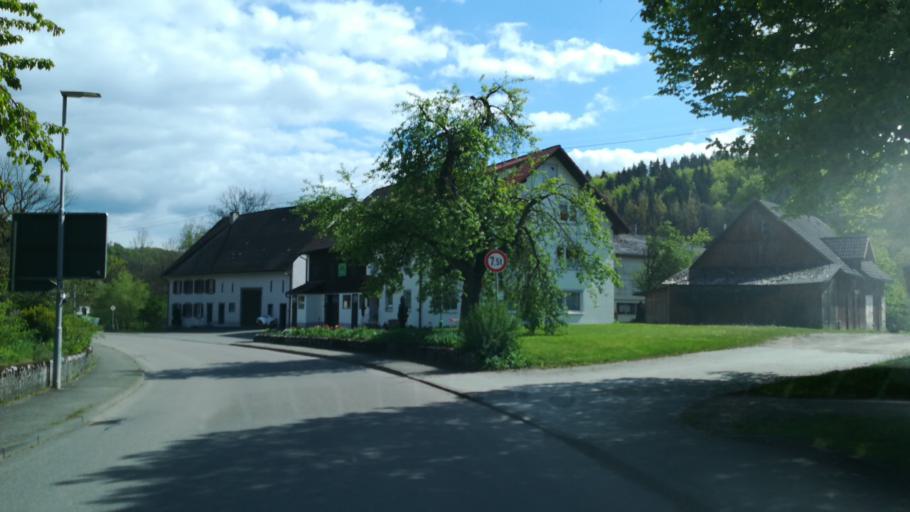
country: DE
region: Baden-Wuerttemberg
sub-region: Freiburg Region
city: Blumberg
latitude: 47.8366
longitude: 8.5016
